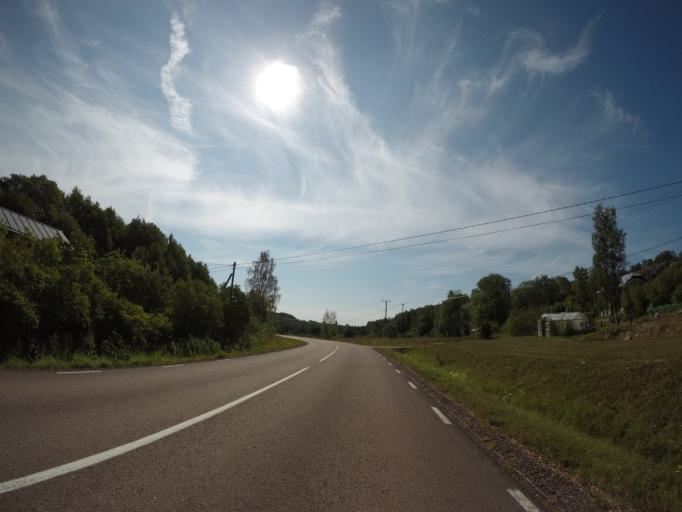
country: AX
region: Alands landsbygd
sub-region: Finstroem
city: Finstroem
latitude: 60.2731
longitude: 19.9210
